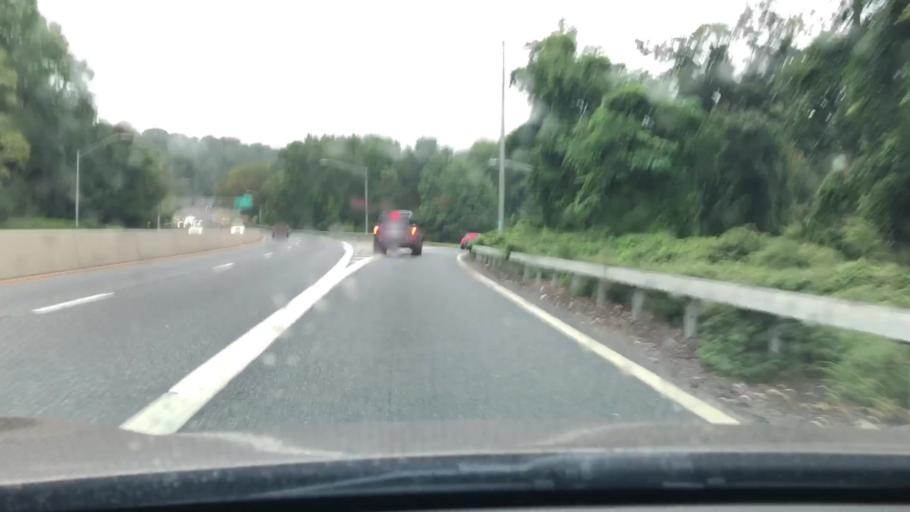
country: US
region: New York
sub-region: Westchester County
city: Yonkers
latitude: 40.9303
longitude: -73.8784
